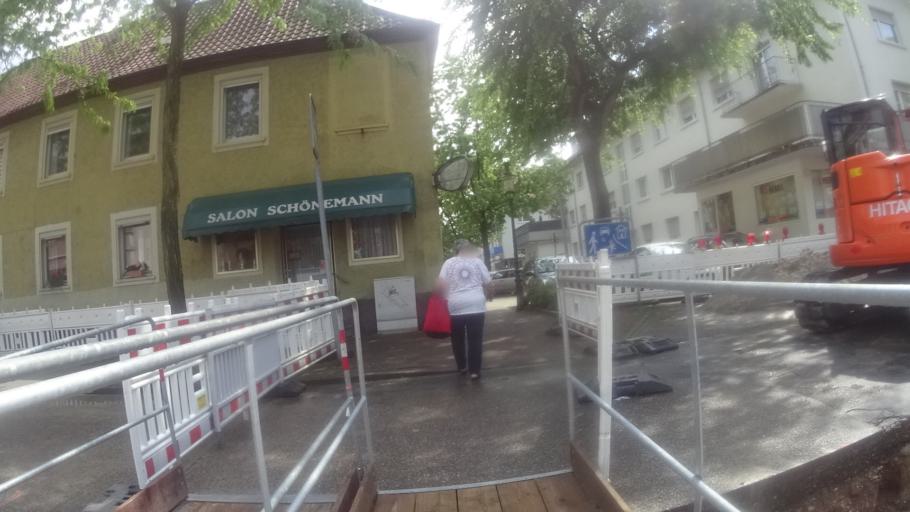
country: DE
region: Baden-Wuerttemberg
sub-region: Karlsruhe Region
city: Rastatt
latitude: 48.8533
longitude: 8.2078
